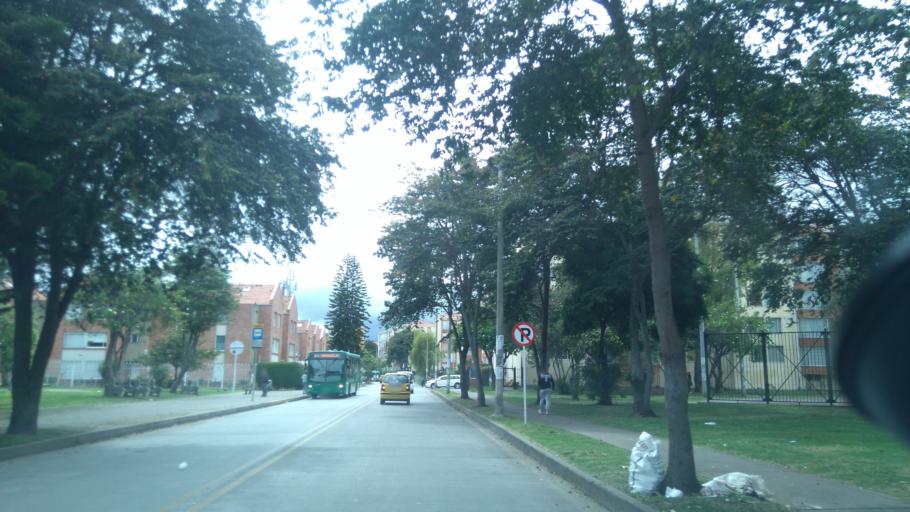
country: CO
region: Cundinamarca
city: Cota
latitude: 4.7646
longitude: -74.0492
